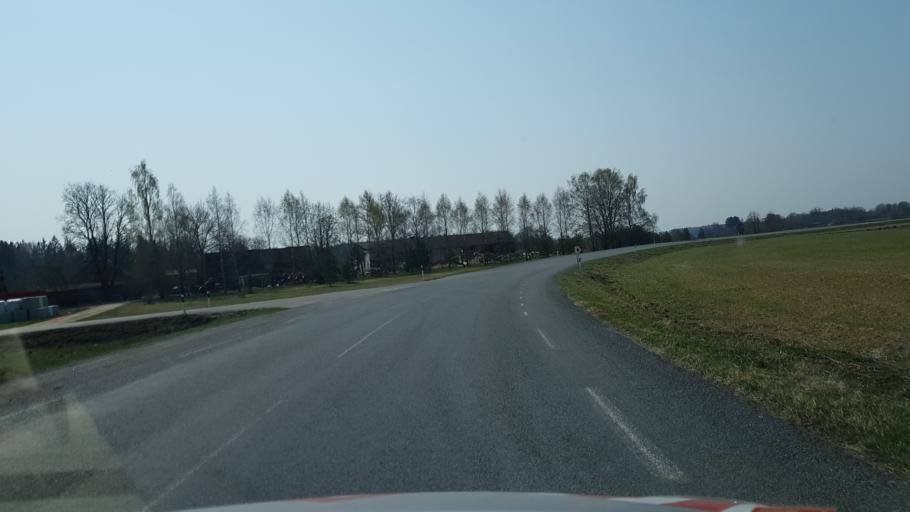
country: EE
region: Raplamaa
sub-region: Kehtna vald
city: Kehtna
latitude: 59.0110
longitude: 24.9198
